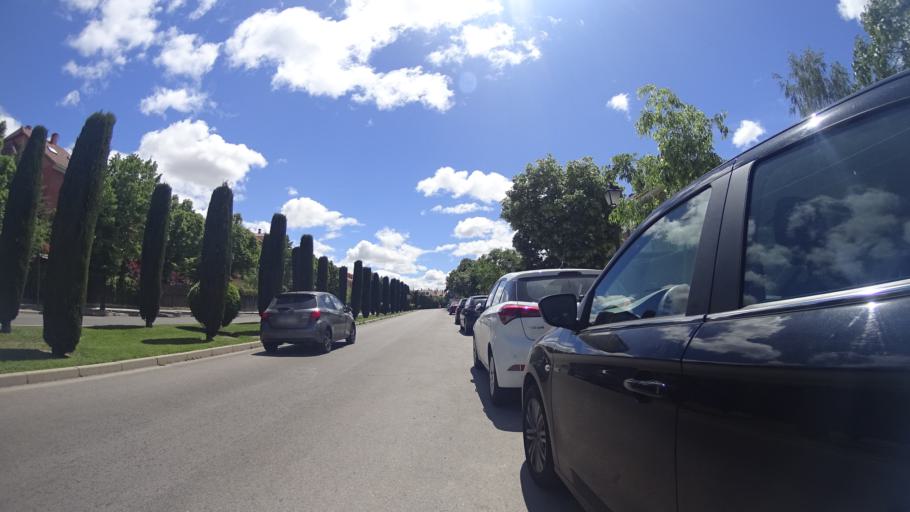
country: ES
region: Madrid
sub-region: Provincia de Madrid
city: Villaviciosa de Odon
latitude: 40.3629
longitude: -3.9136
